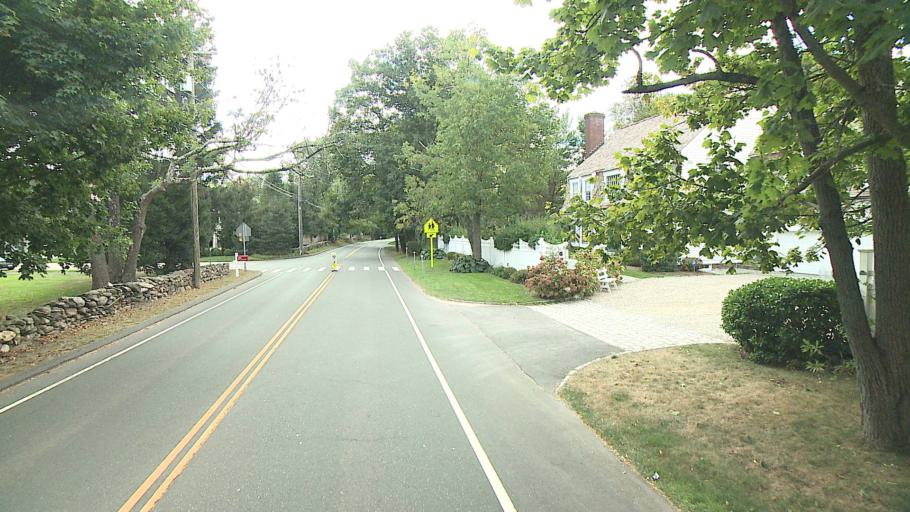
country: US
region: Connecticut
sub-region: Fairfield County
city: New Canaan
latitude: 41.1323
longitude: -73.4955
